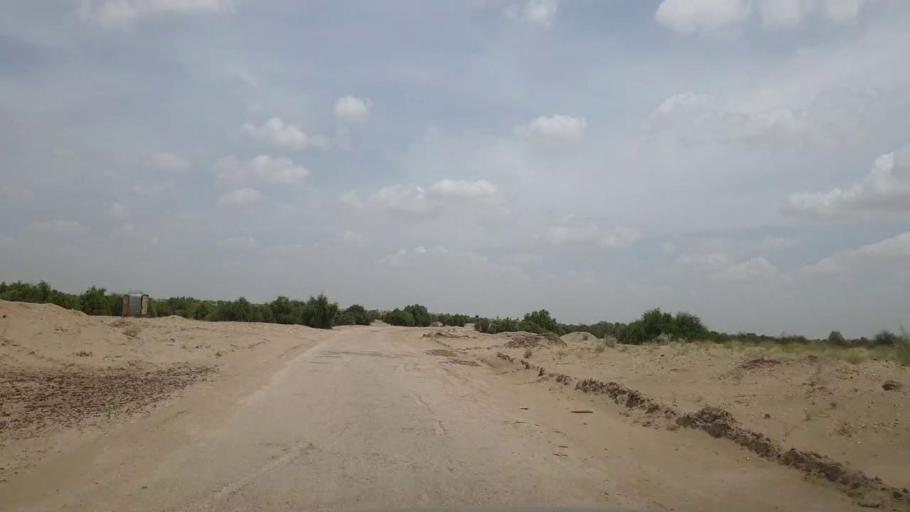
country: PK
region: Sindh
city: Kot Diji
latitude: 27.1937
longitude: 69.1641
